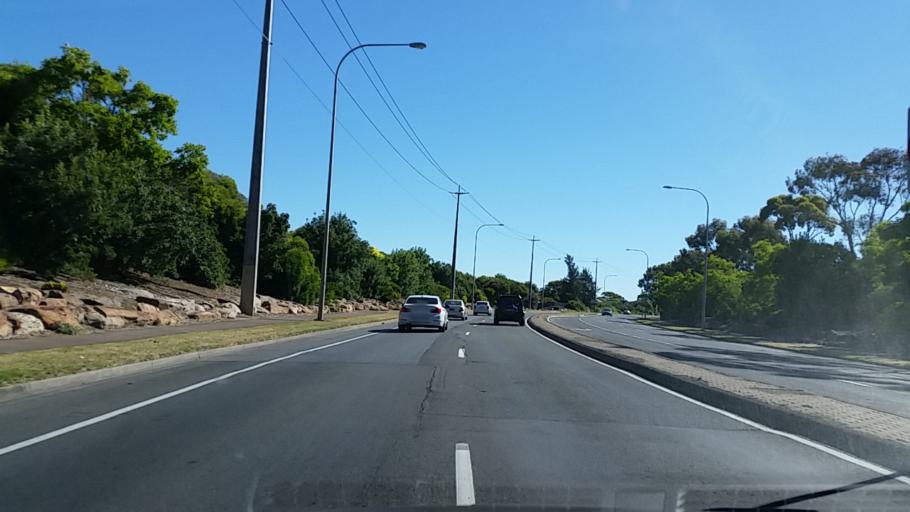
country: AU
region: South Australia
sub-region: Tea Tree Gully
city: Modbury
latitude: -34.8044
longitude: 138.6843
